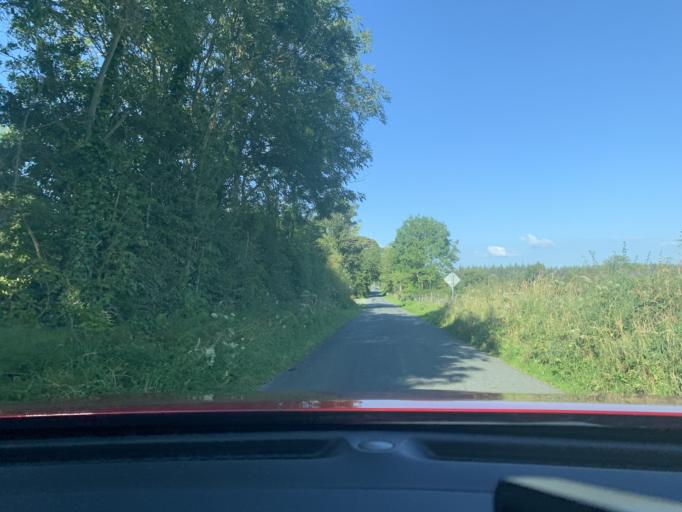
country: IE
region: Connaught
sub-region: Sligo
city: Tobercurry
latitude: 54.1236
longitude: -8.7422
